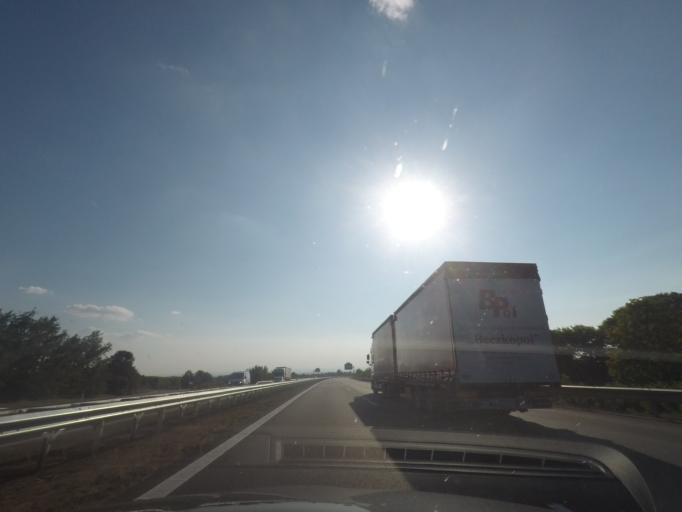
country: CZ
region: Olomoucky
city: Praslavice
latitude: 49.5786
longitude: 17.3909
